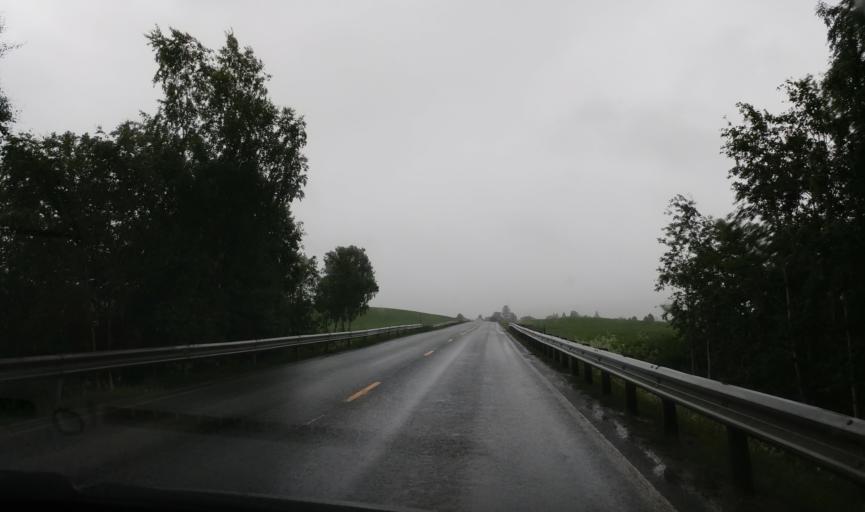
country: NO
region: Nord-Trondelag
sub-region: Stjordal
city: Stjordalshalsen
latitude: 63.4241
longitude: 10.9287
